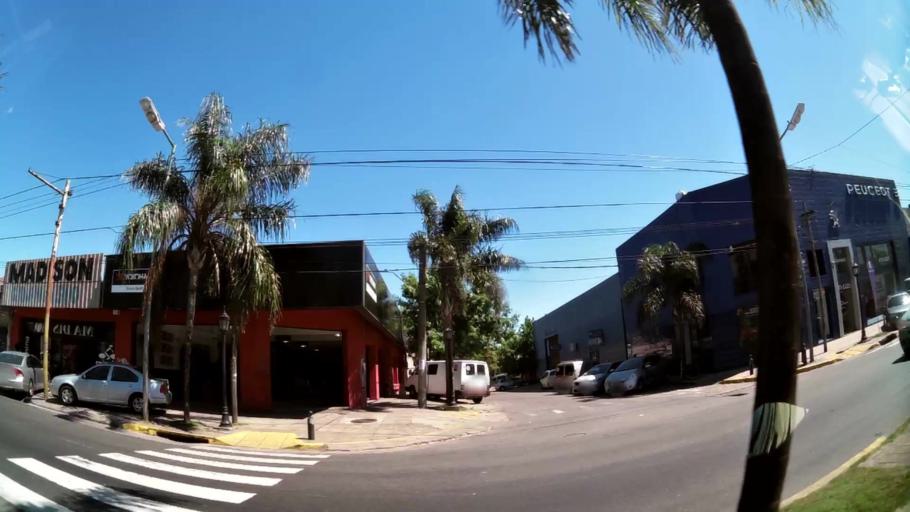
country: AR
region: Buenos Aires
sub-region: Partido de Tigre
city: Tigre
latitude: -34.4970
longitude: -58.6369
